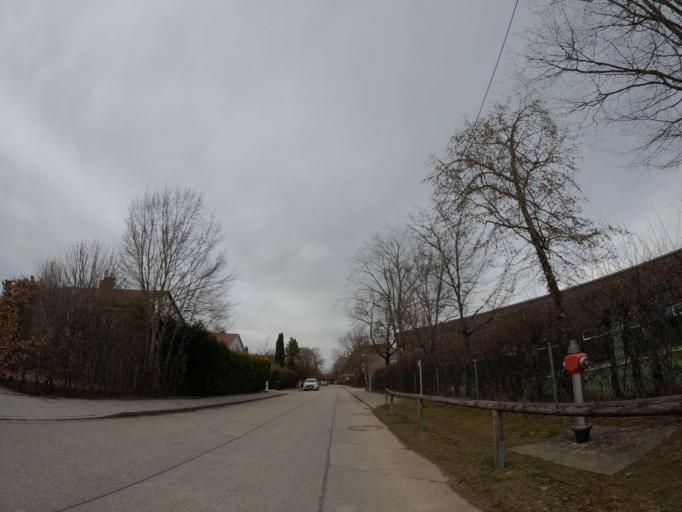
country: DE
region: Bavaria
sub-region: Upper Bavaria
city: Oberhaching
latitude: 48.0193
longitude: 11.5778
